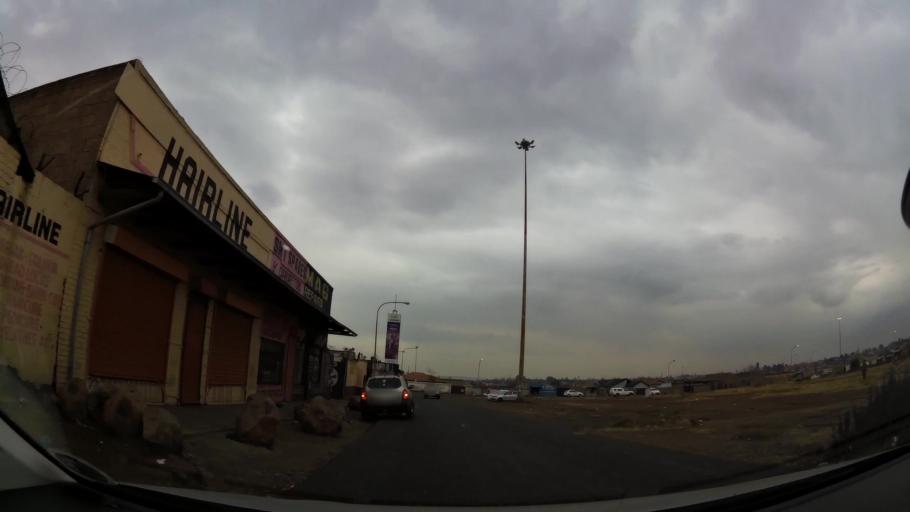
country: ZA
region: Gauteng
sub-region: City of Johannesburg Metropolitan Municipality
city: Soweto
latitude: -26.2549
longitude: 27.8746
